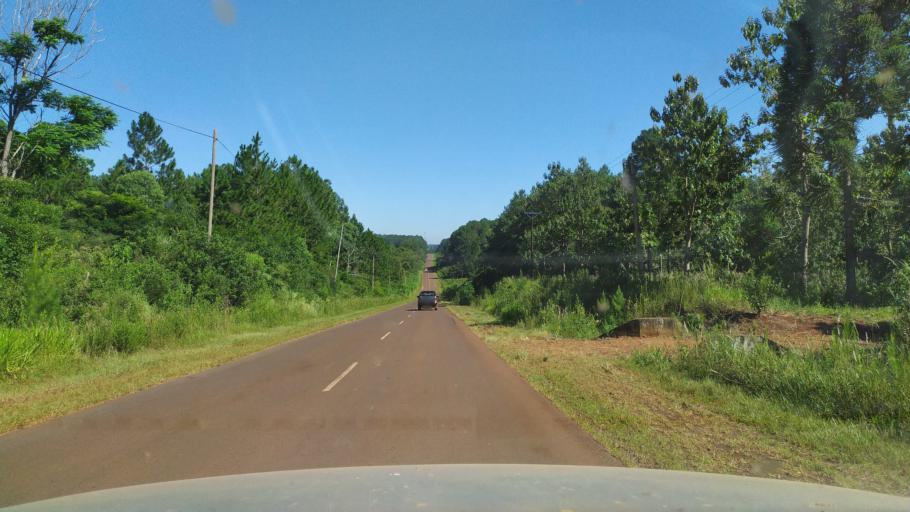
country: AR
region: Misiones
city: Caraguatay
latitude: -26.6691
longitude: -54.7274
